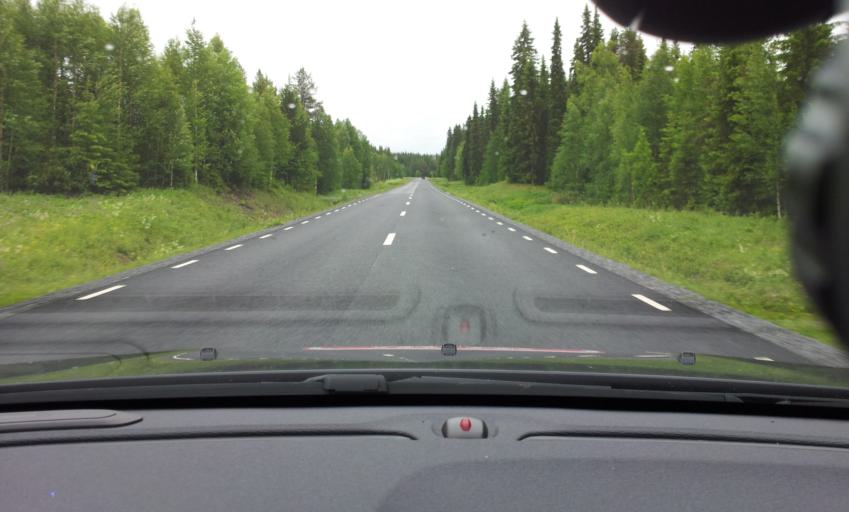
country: SE
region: Jaemtland
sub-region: Stroemsunds Kommun
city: Stroemsund
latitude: 63.6363
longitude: 15.1940
